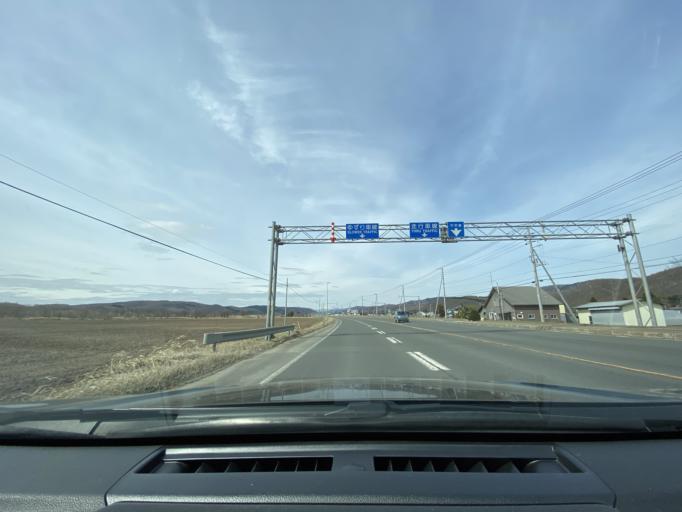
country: JP
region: Hokkaido
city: Kitami
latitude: 43.7950
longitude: 143.7316
